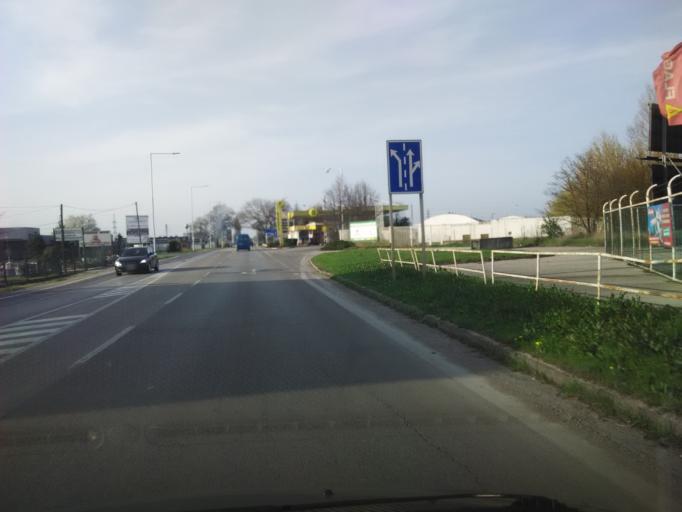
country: SK
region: Nitriansky
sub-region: Okres Nove Zamky
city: Nove Zamky
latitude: 48.0083
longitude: 18.1563
